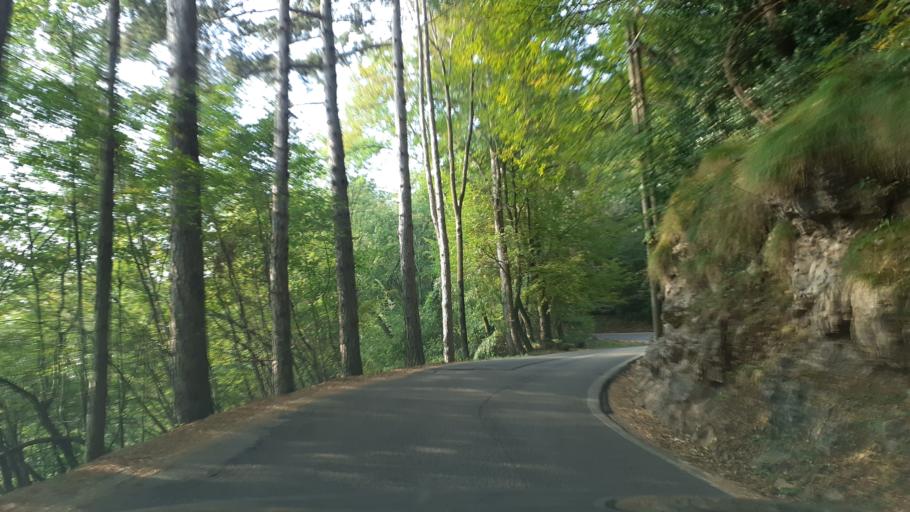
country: IT
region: Lombardy
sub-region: Provincia di Lecco
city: Ballabio
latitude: 45.8991
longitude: 9.4130
